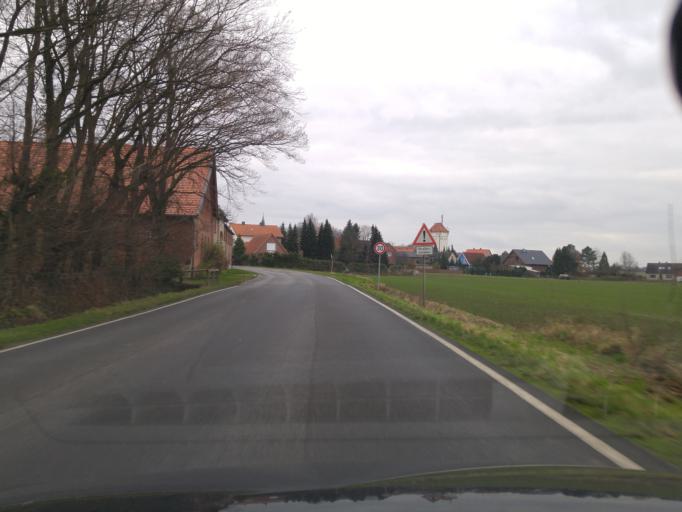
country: DE
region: Lower Saxony
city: Ilsede
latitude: 52.2126
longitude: 10.1759
